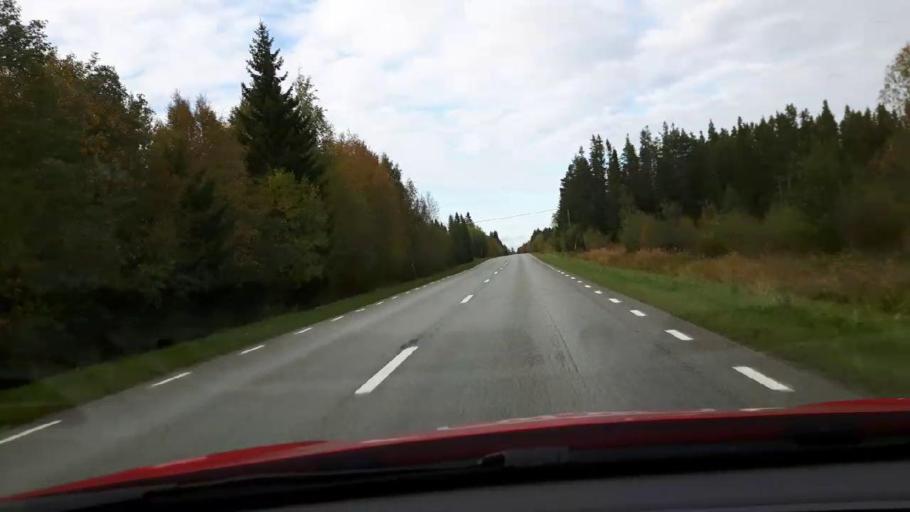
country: SE
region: Jaemtland
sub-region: Krokoms Kommun
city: Valla
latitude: 63.2288
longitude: 14.0144
